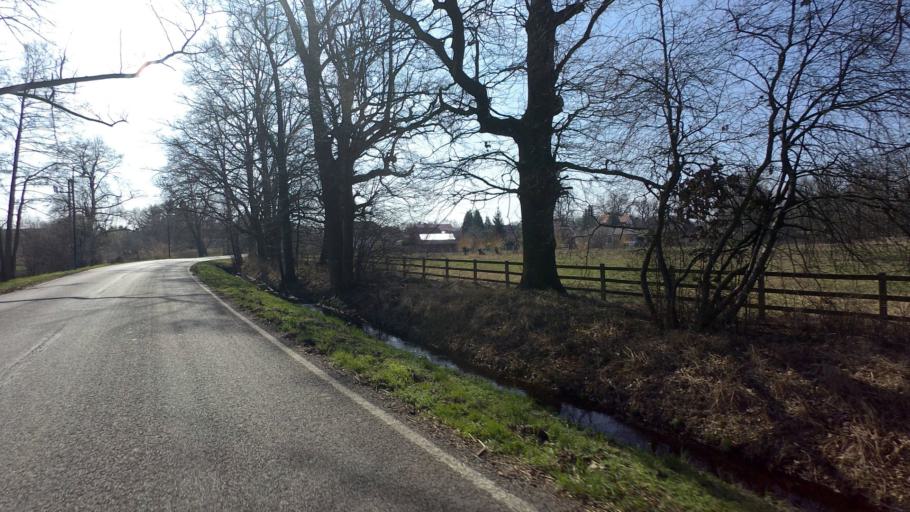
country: DE
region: Brandenburg
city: Sperenberg
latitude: 52.0492
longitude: 13.3207
